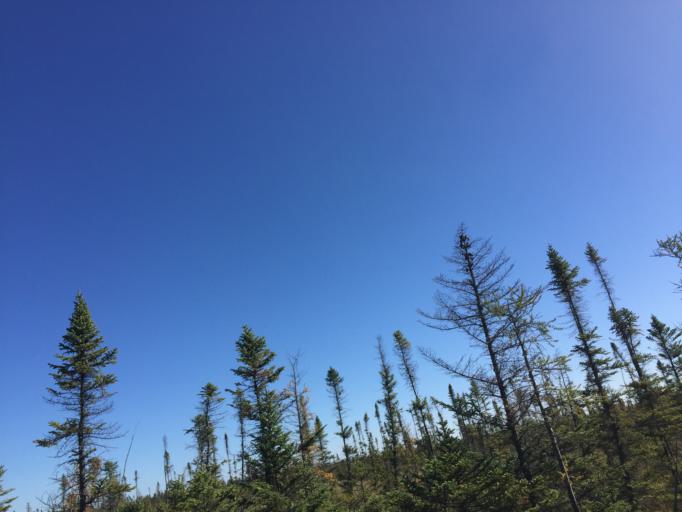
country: US
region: Minnesota
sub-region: Lake of the Woods County
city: Baudette
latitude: 48.2984
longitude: -94.5675
